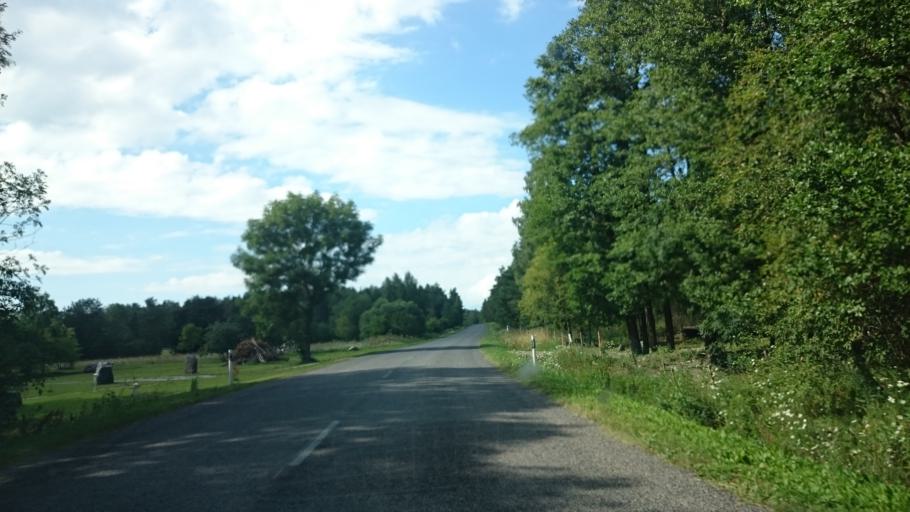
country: EE
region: Saare
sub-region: Orissaare vald
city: Orissaare
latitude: 58.6020
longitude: 22.9755
